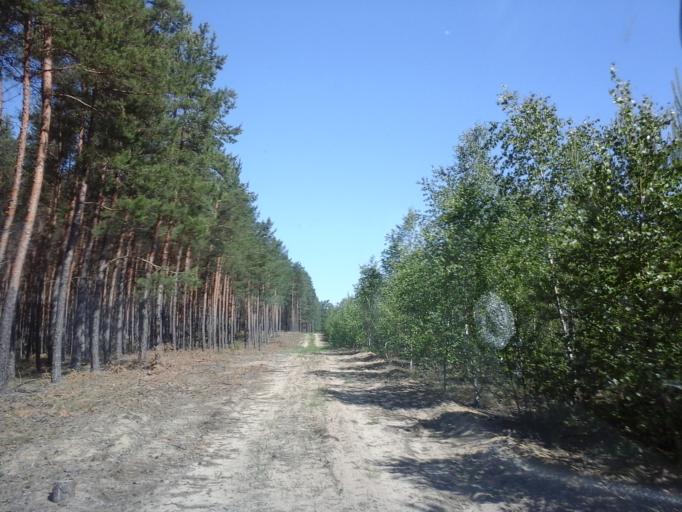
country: PL
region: West Pomeranian Voivodeship
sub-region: Powiat drawski
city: Kalisz Pomorski
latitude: 53.1872
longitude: 15.9583
